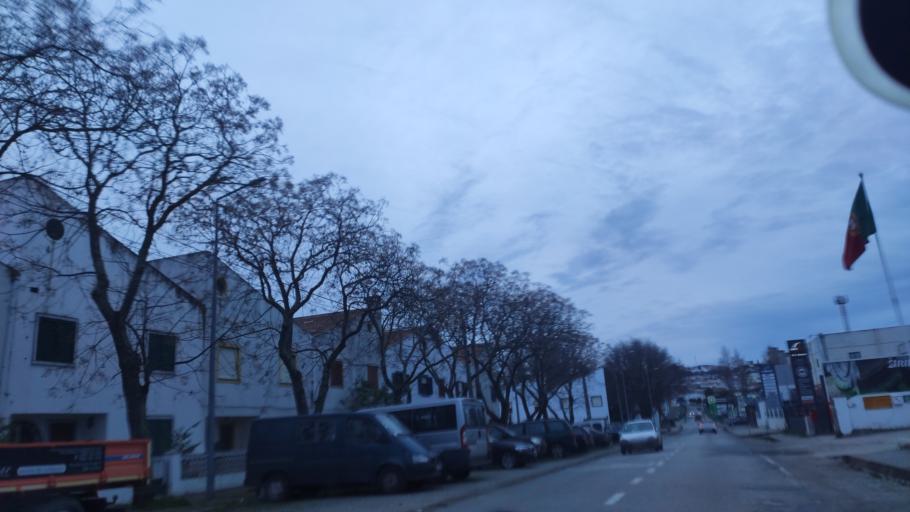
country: PT
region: Beja
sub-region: Beja
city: Beja
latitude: 38.0197
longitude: -7.8509
